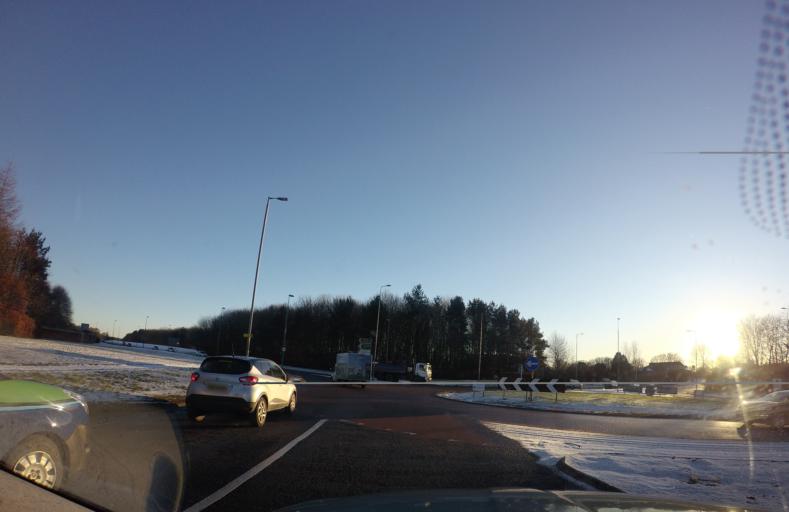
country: GB
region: Scotland
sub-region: Angus
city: Muirhead
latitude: 56.4651
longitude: -3.0624
